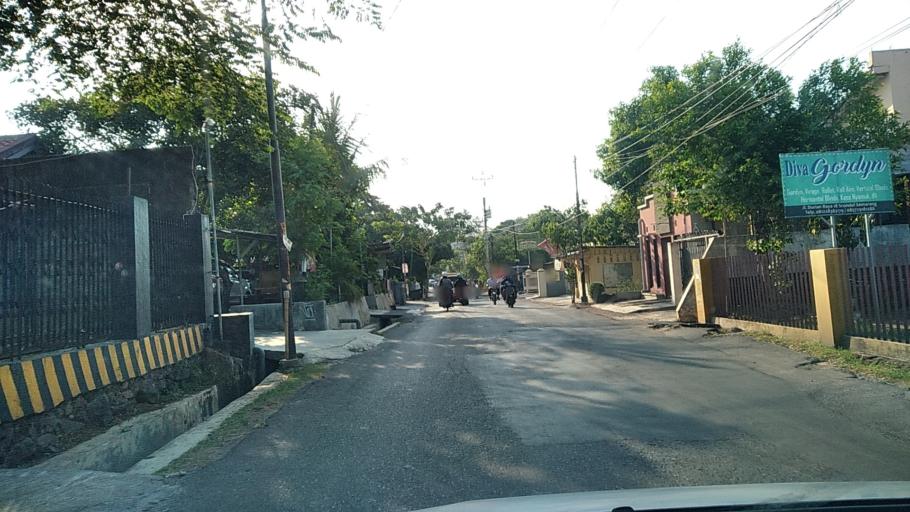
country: ID
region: Central Java
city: Semarang
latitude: -7.0612
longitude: 110.4160
